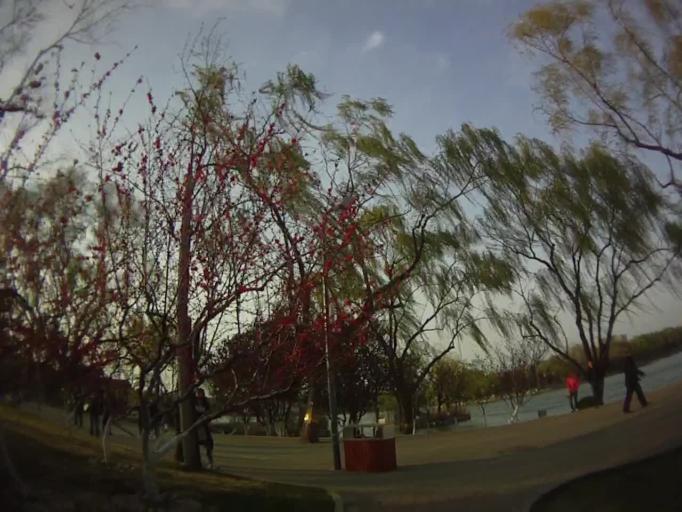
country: CN
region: Beijing
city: Longtan
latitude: 39.8750
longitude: 116.4348
